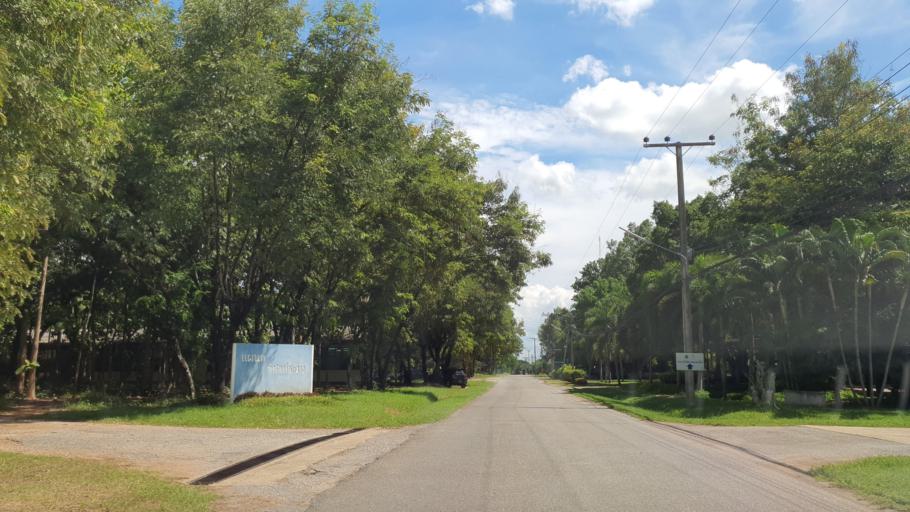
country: TH
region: Chiang Mai
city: San Pa Tong
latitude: 18.5819
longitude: 98.8742
